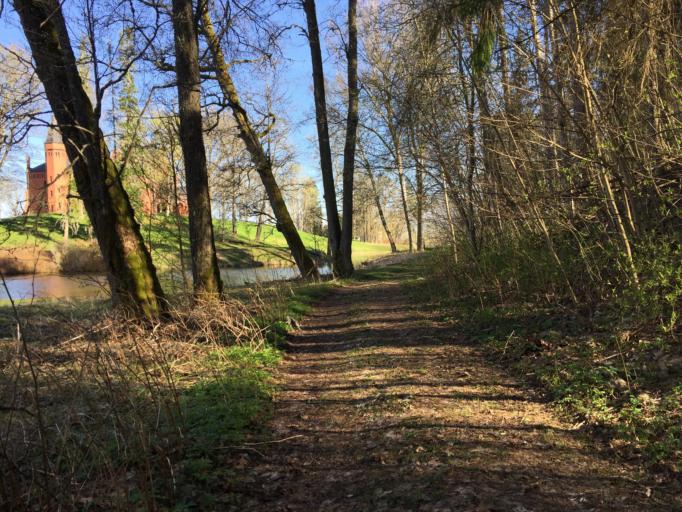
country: EE
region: Vorumaa
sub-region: Antsla vald
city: Vana-Antsla
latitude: 57.9024
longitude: 26.2777
